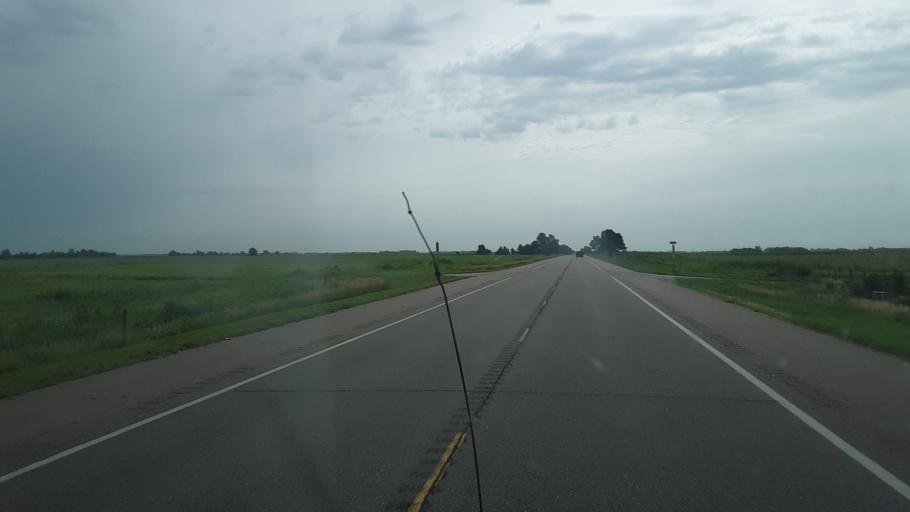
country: US
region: Kansas
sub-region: Stafford County
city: Saint John
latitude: 37.9560
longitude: -98.7851
